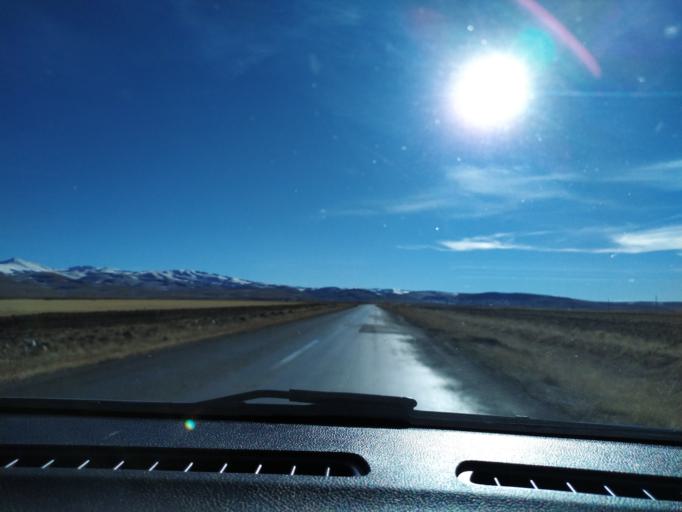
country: TR
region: Kayseri
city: Orensehir
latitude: 38.8857
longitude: 36.7282
